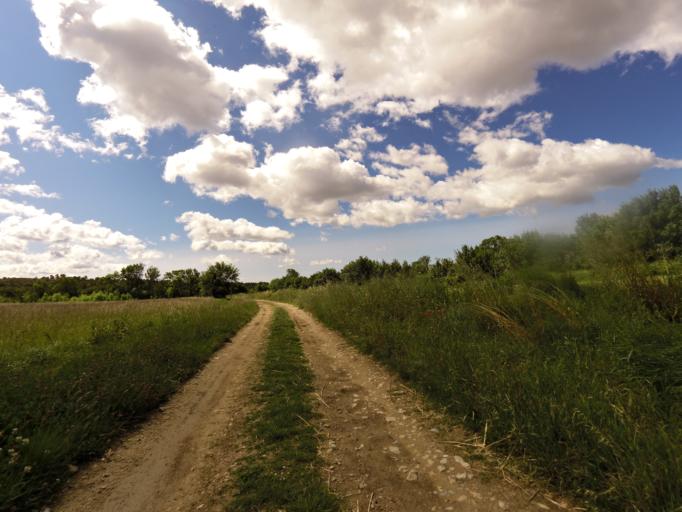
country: FR
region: Languedoc-Roussillon
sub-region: Departement du Gard
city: Vergeze
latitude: 43.7629
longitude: 4.2128
